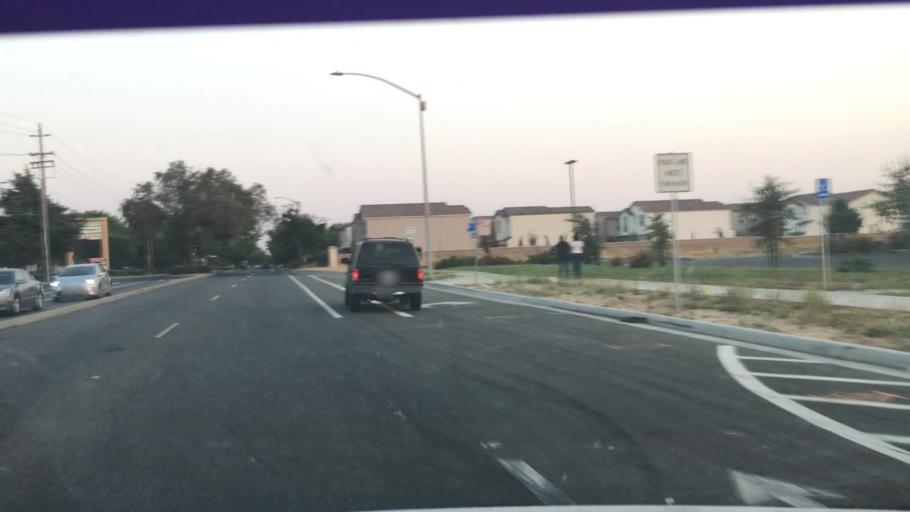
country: US
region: California
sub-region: Sacramento County
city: Parkway
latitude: 38.4741
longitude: -121.4504
